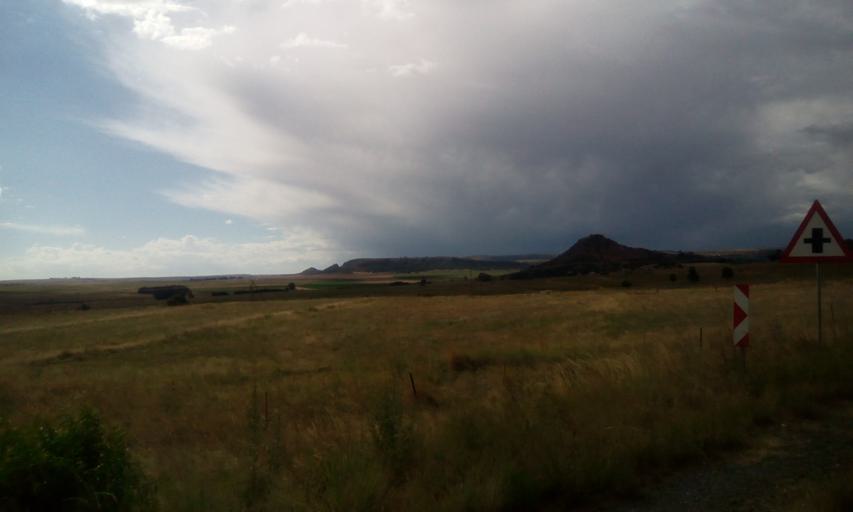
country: LS
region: Maseru
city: Maseru
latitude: -29.2683
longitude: 27.4344
